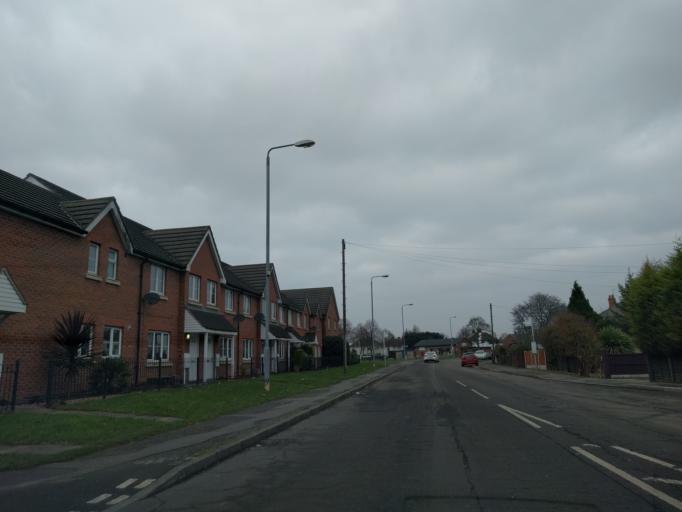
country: GB
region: England
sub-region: Nottinghamshire
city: Newark on Trent
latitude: 53.0860
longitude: -0.7993
